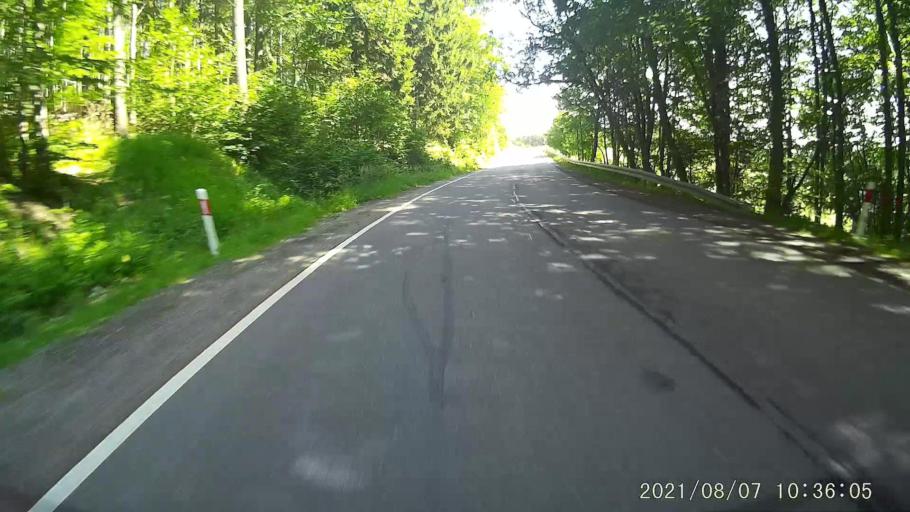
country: PL
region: Lower Silesian Voivodeship
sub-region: Powiat klodzki
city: Duszniki-Zdroj
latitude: 50.3641
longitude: 16.3696
